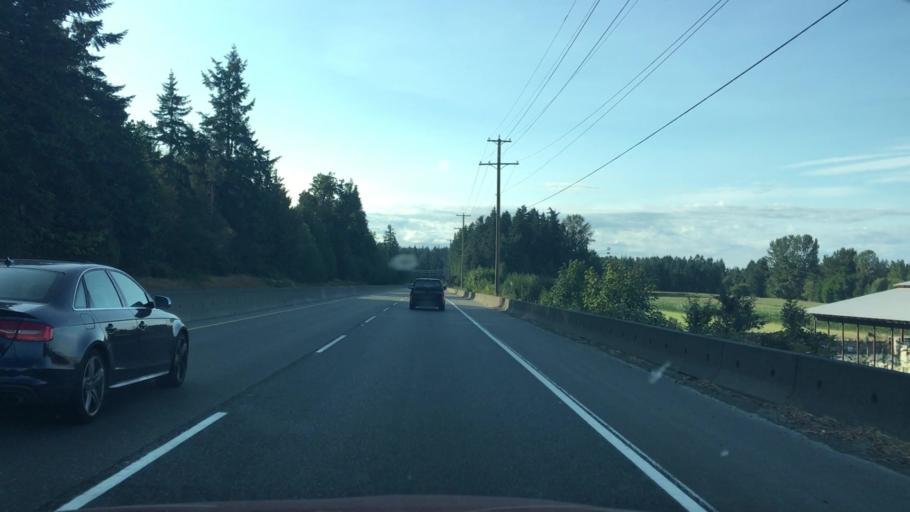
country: CA
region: British Columbia
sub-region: Cowichan Valley Regional District
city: Ladysmith
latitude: 48.9432
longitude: -123.7697
